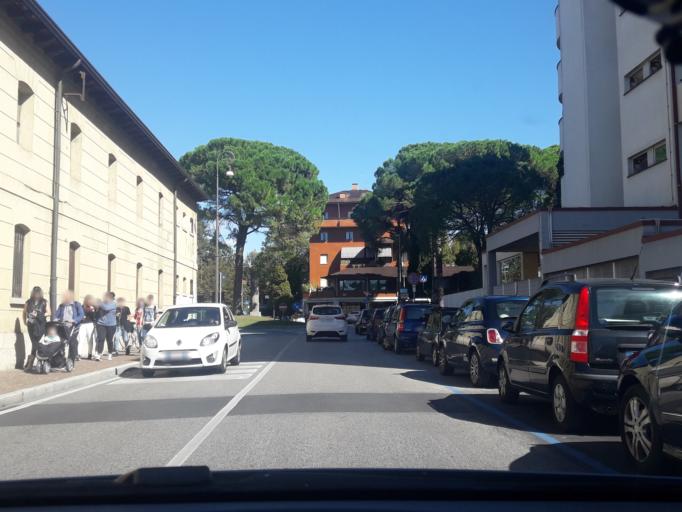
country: IT
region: Friuli Venezia Giulia
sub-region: Provincia di Udine
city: Udine
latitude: 46.0688
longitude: 13.2392
